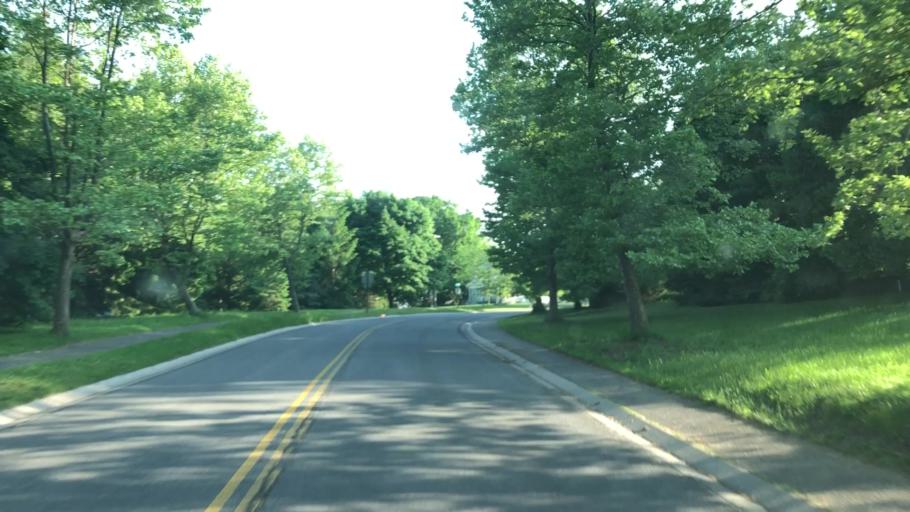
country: US
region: New York
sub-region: Wayne County
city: Macedon
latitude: 43.1229
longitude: -77.3066
